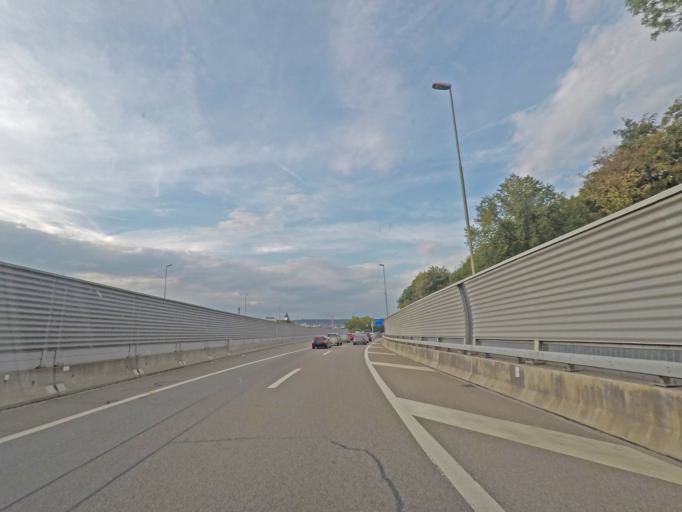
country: CH
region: Zurich
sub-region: Bezirk Zuerich
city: Zuerich (Kreis 3) / Alt-Wiedikon
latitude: 47.3625
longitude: 8.5229
